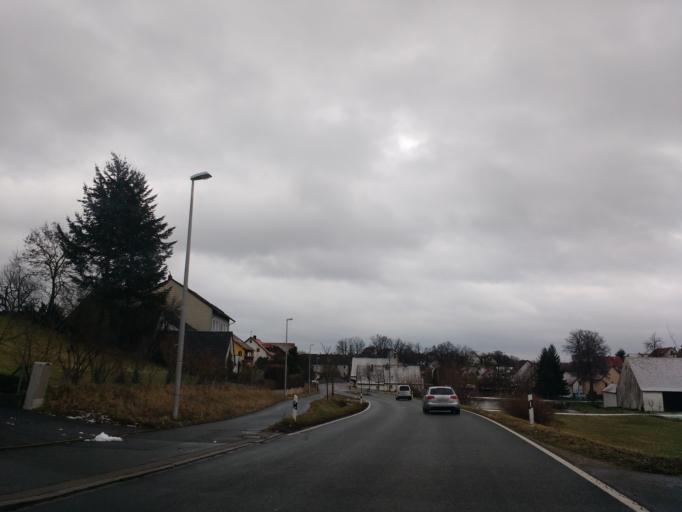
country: DE
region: Bavaria
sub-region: Regierungsbezirk Mittelfranken
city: Herzogenaurach
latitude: 49.5865
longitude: 10.8579
